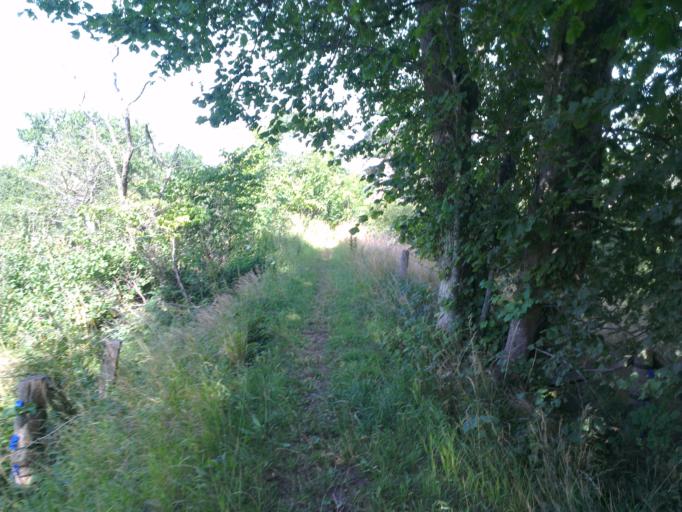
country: DK
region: Capital Region
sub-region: Frederikssund Kommune
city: Frederikssund
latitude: 55.7766
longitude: 12.0323
